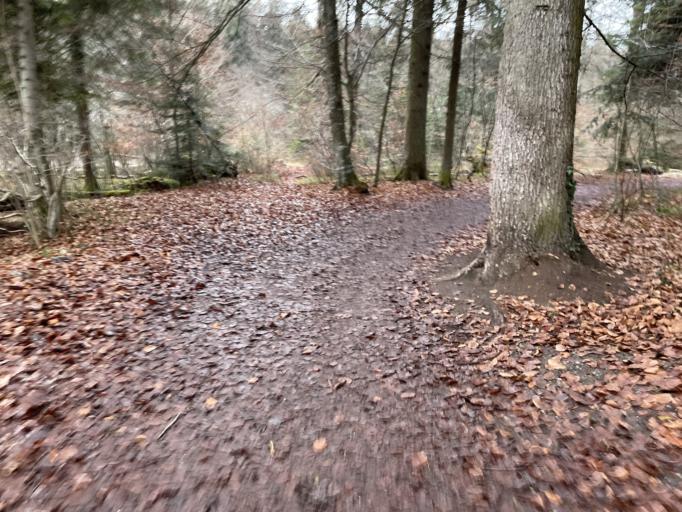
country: CH
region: Bern
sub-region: Thun District
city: Uttigen
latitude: 46.8082
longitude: 7.5694
